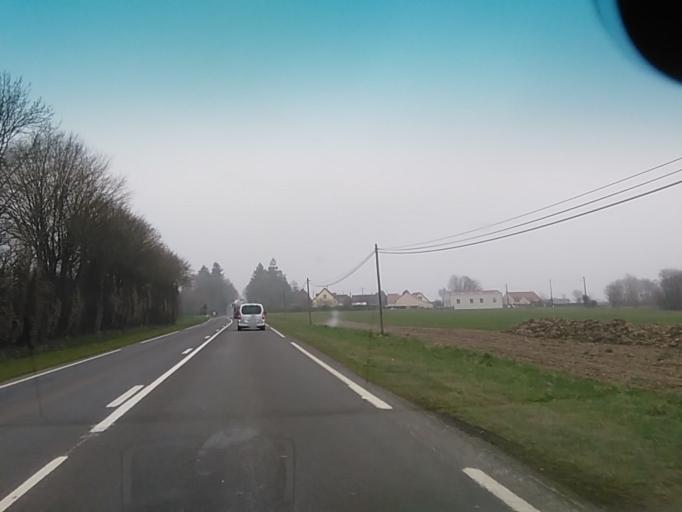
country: FR
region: Lower Normandy
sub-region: Departement de l'Orne
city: Magny-le-Desert
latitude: 48.6369
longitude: -0.2207
